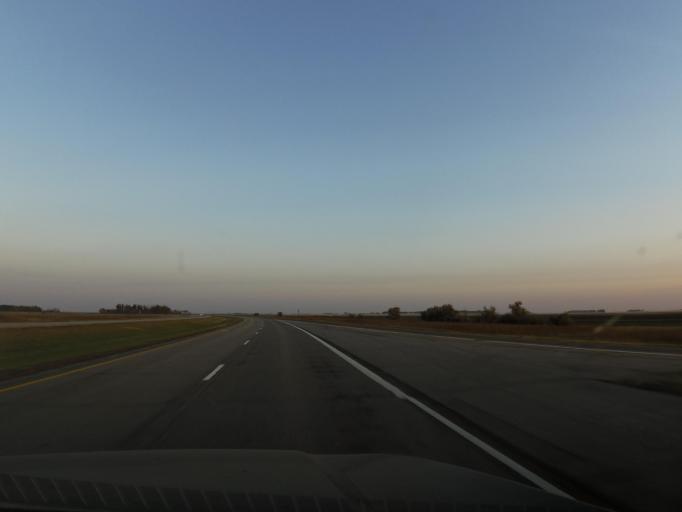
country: US
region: Minnesota
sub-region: Kittson County
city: Hallock
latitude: 48.7580
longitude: -97.2098
